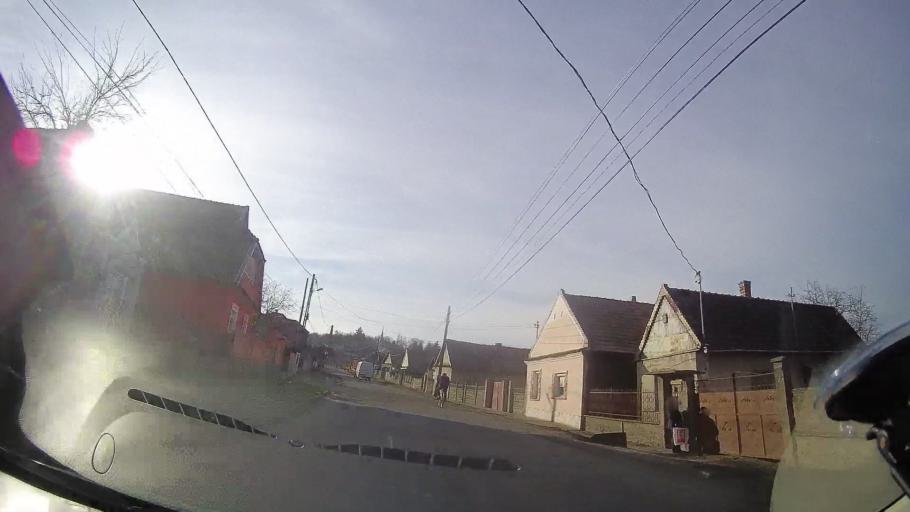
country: RO
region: Bihor
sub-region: Comuna Spinus
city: Spinus
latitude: 47.2017
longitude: 22.1915
